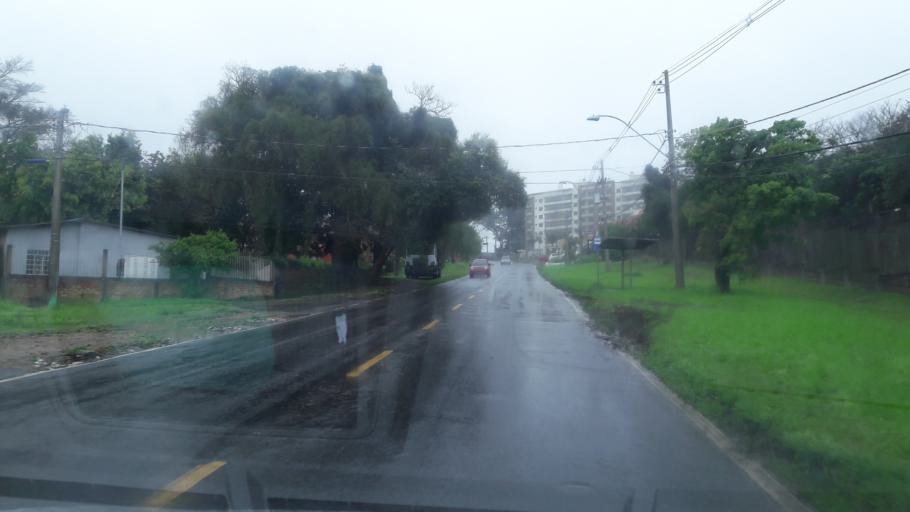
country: BR
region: Rio Grande do Sul
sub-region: Porto Alegre
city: Porto Alegre
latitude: -30.1287
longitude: -51.2234
